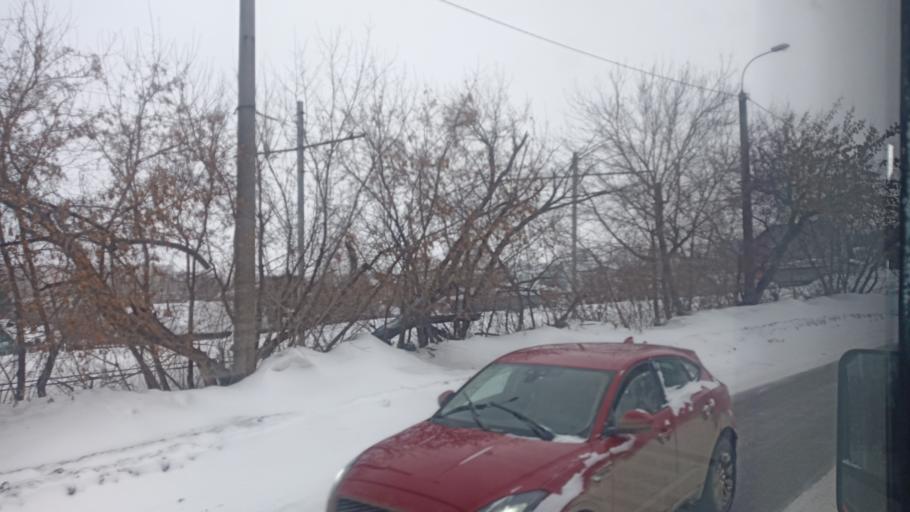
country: RU
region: Altai Krai
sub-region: Gorod Barnaulskiy
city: Barnaul
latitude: 53.3876
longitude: 83.6813
